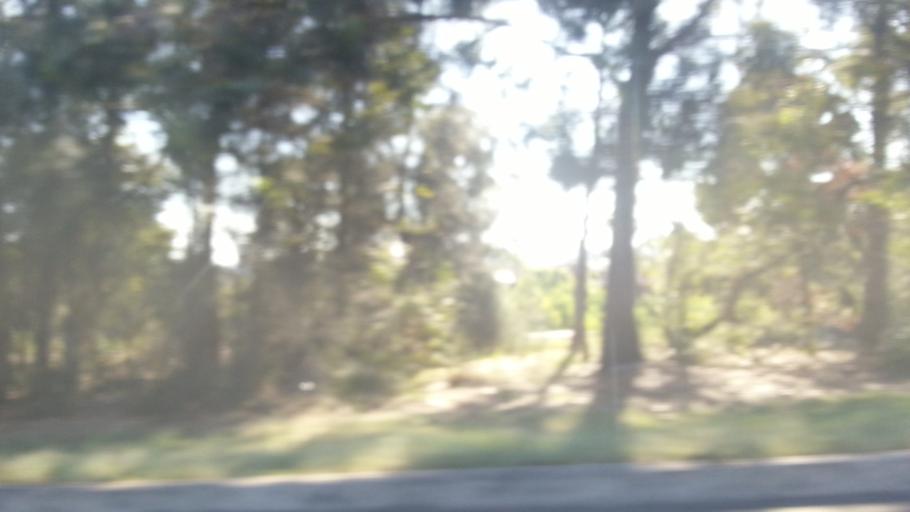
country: AU
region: New South Wales
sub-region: Wollongong
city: Berkeley
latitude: -34.4776
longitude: 150.8552
